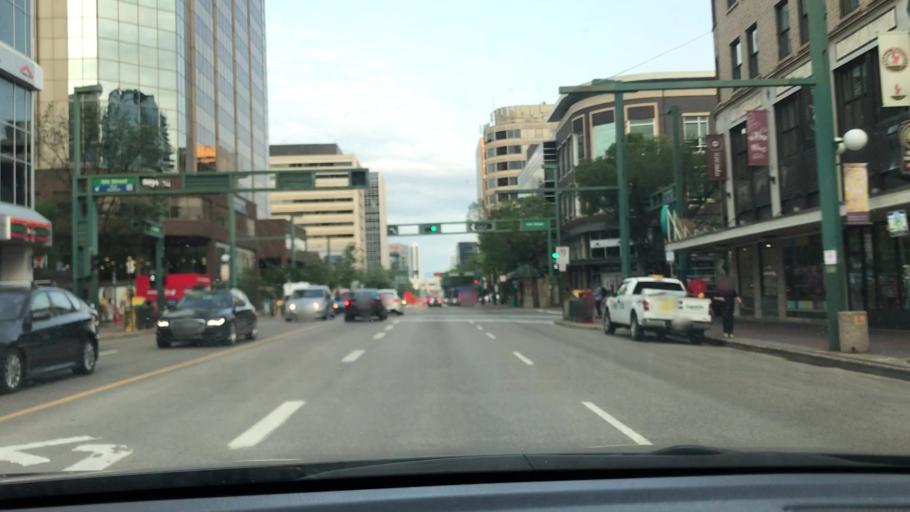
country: CA
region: Alberta
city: Edmonton
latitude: 53.5409
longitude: -113.4985
